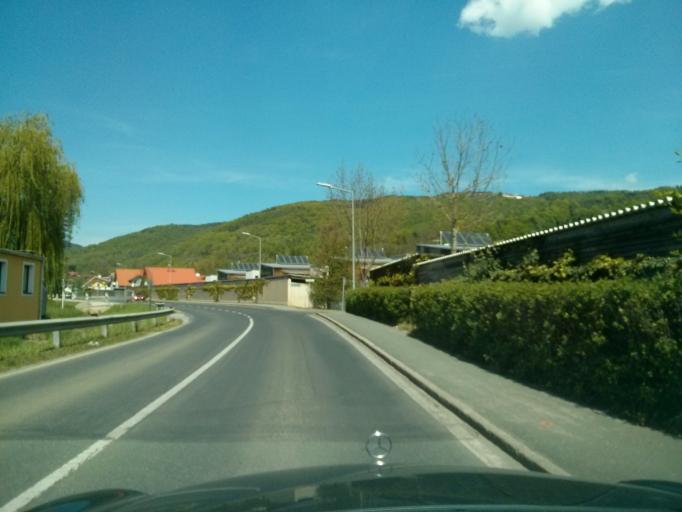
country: AT
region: Styria
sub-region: Politischer Bezirk Graz-Umgebung
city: Stattegg
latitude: 47.1279
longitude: 15.4253
